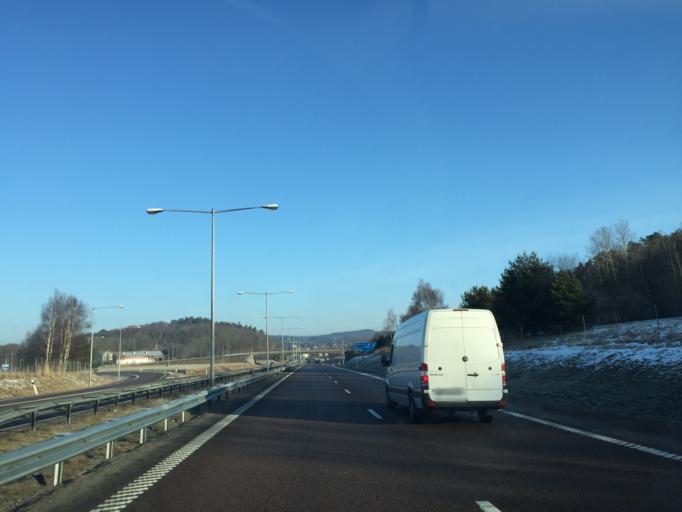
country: SE
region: Vaestra Goetaland
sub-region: Uddevalla Kommun
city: Ljungskile
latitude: 58.2102
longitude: 11.9129
